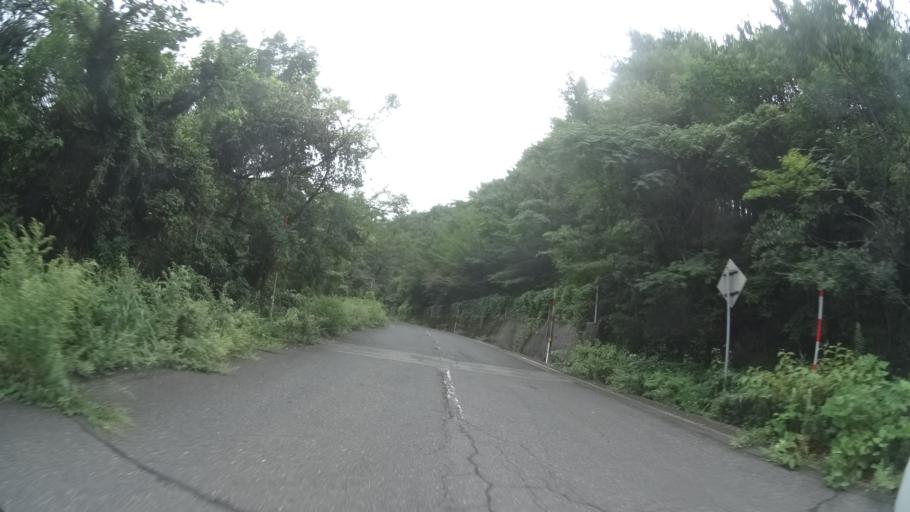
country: JP
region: Tottori
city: Kurayoshi
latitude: 35.4019
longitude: 134.0027
